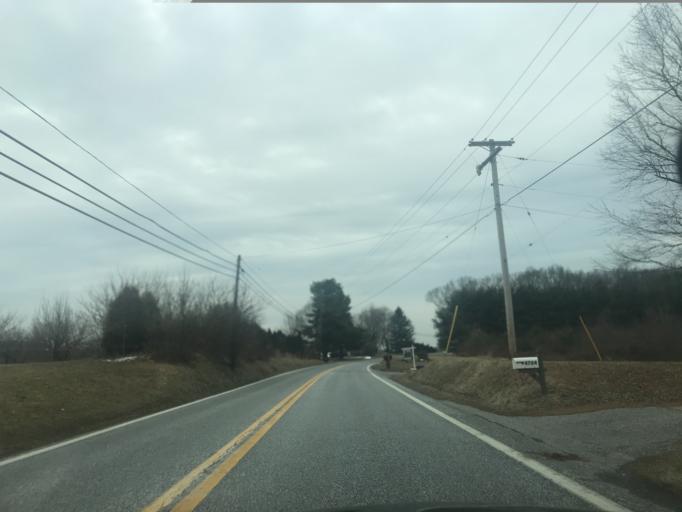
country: US
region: Maryland
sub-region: Harford County
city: Jarrettsville
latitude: 39.6603
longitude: -76.5441
